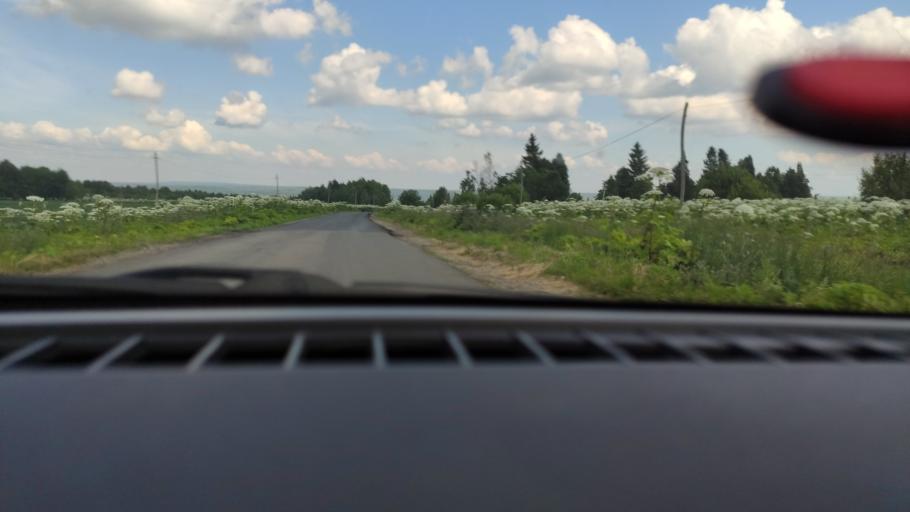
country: RU
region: Perm
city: Sylva
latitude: 58.0299
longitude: 56.7206
